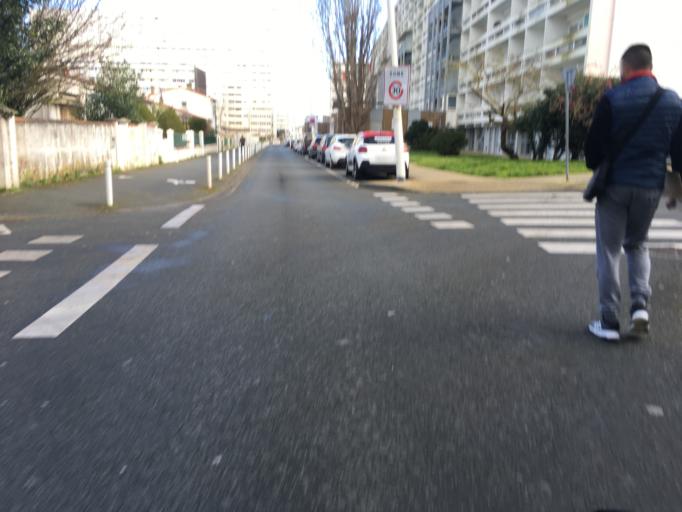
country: FR
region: Poitou-Charentes
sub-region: Departement de la Charente-Maritime
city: La Rochelle
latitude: 46.1674
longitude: -1.1777
